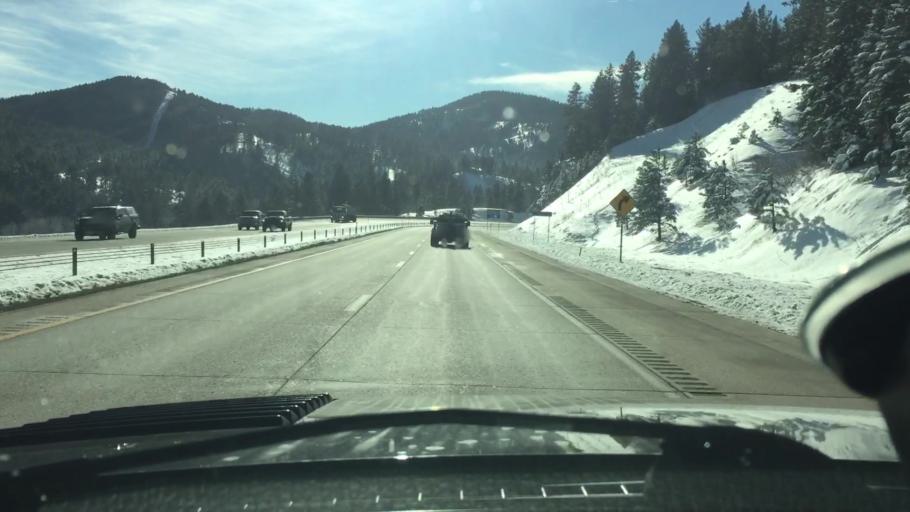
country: US
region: Colorado
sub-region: Jefferson County
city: Indian Hills
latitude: 39.5965
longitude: -105.2245
